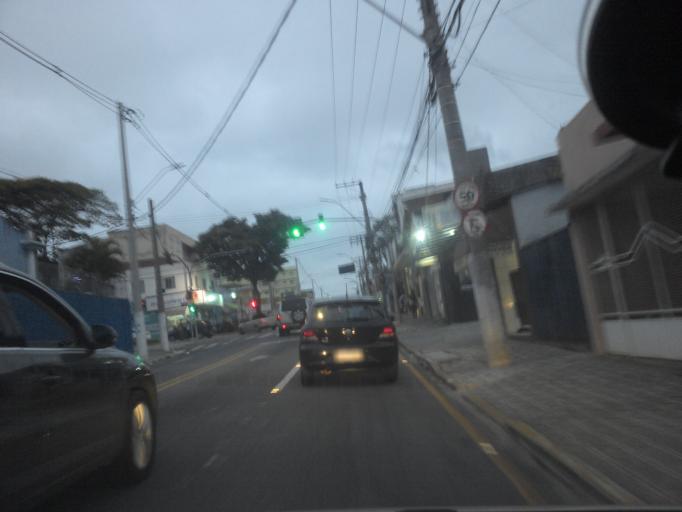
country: BR
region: Sao Paulo
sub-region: Taubate
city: Taubate
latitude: -23.0224
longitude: -45.5473
